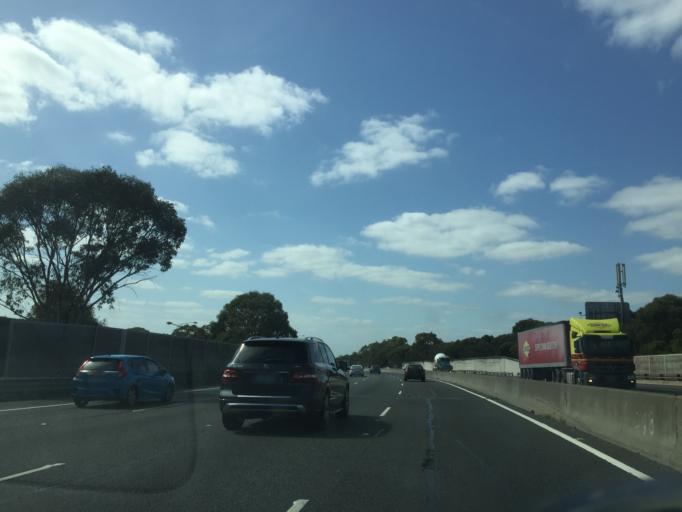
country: AU
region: New South Wales
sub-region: Holroyd
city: Merrylands
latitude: -33.8238
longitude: 150.9876
